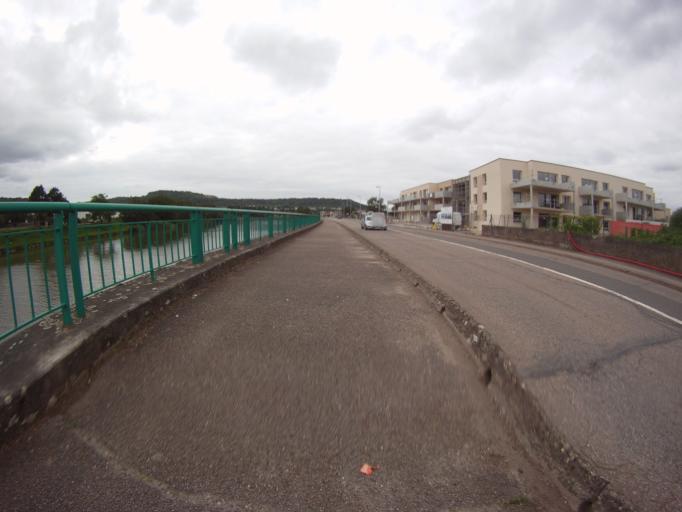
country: FR
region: Lorraine
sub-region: Departement de Meurthe-et-Moselle
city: Malzeville
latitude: 48.7108
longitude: 6.1791
